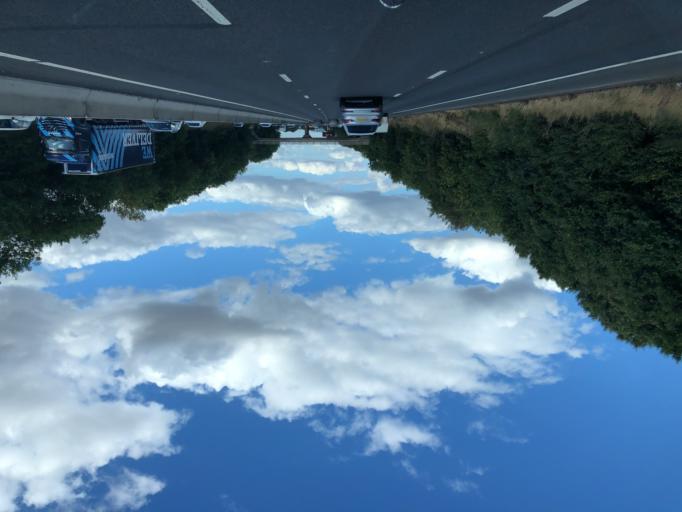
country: GB
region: England
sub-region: Northamptonshire
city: Bugbrooke
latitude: 52.2224
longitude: -0.9795
